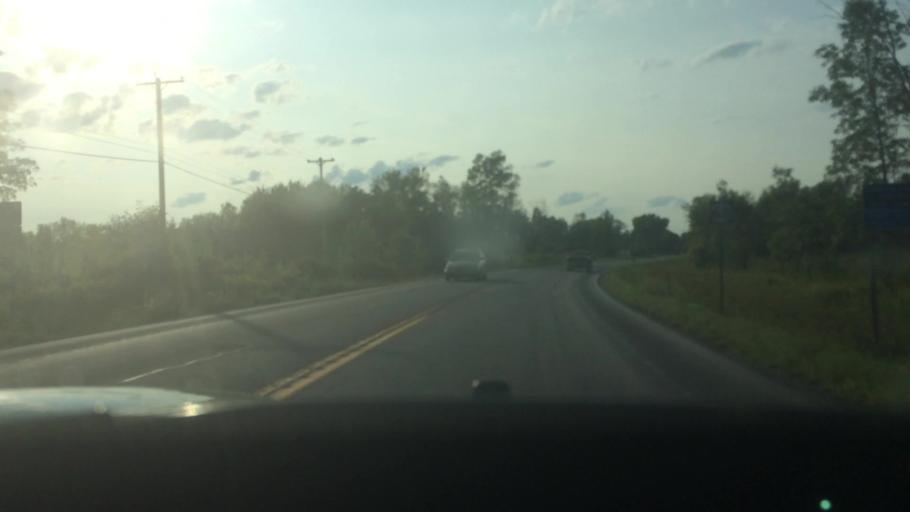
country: US
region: New York
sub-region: St. Lawrence County
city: Ogdensburg
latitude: 44.6727
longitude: -75.4307
